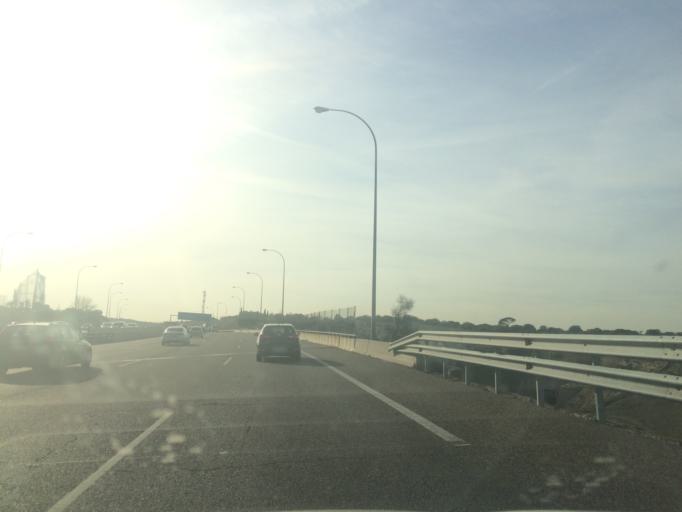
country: ES
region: Madrid
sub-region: Provincia de Madrid
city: Fuencarral-El Pardo
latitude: 40.4933
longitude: -3.7343
